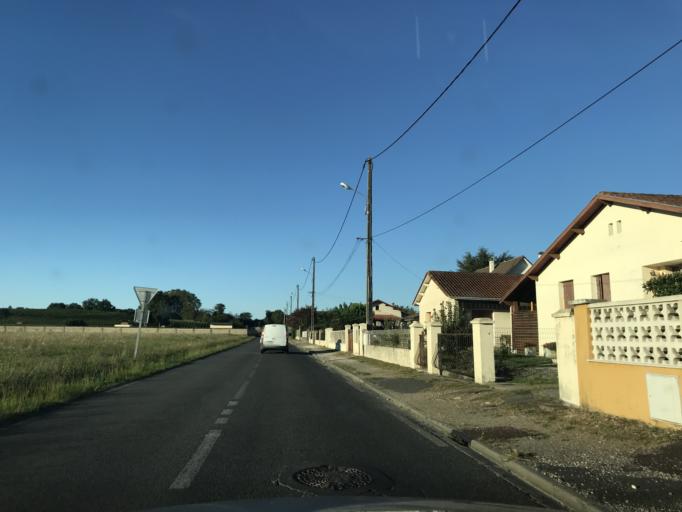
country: FR
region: Aquitaine
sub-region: Departement de la Gironde
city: Mouliets-et-Villemartin
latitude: 44.8614
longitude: -0.0560
